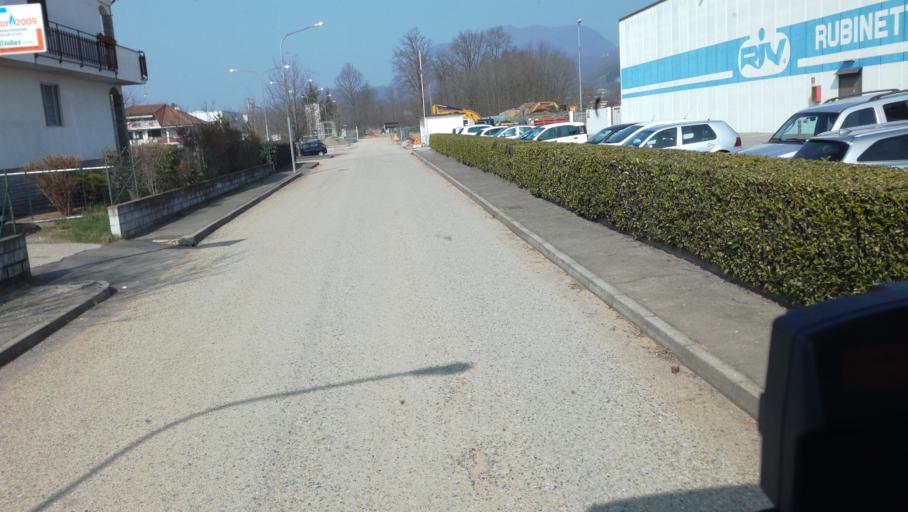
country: IT
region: Piedmont
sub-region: Provincia di Novara
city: Grignasco
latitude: 45.6732
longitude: 8.3517
